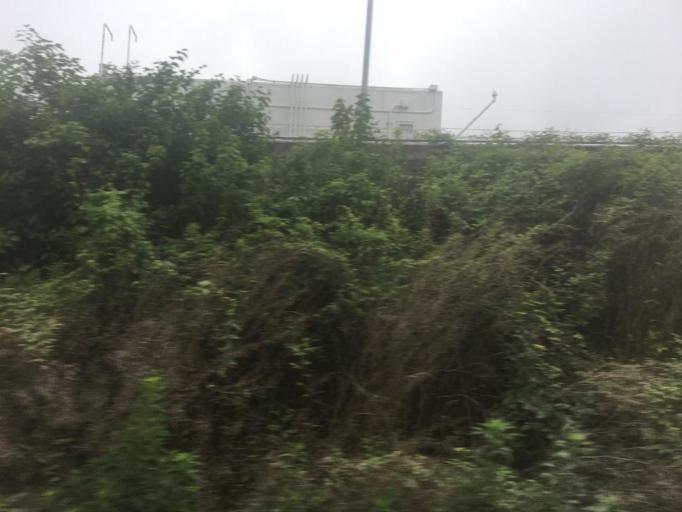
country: JP
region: Chiba
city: Yotsukaido
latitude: 35.7206
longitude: 140.1511
